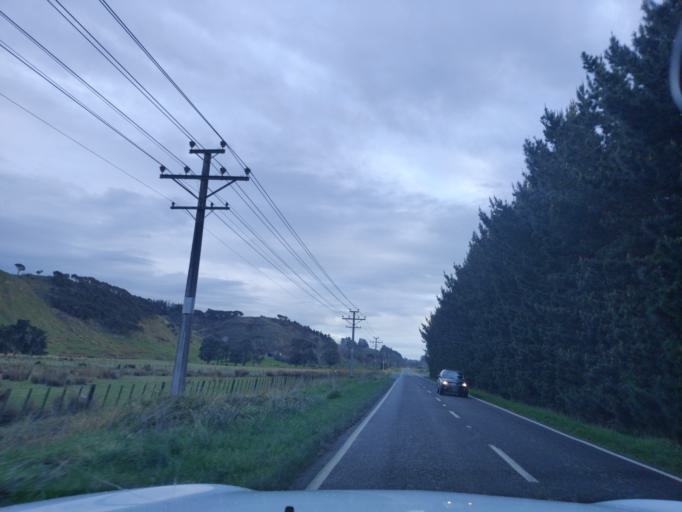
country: NZ
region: Manawatu-Wanganui
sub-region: Palmerston North City
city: Palmerston North
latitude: -40.3596
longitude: 175.6801
